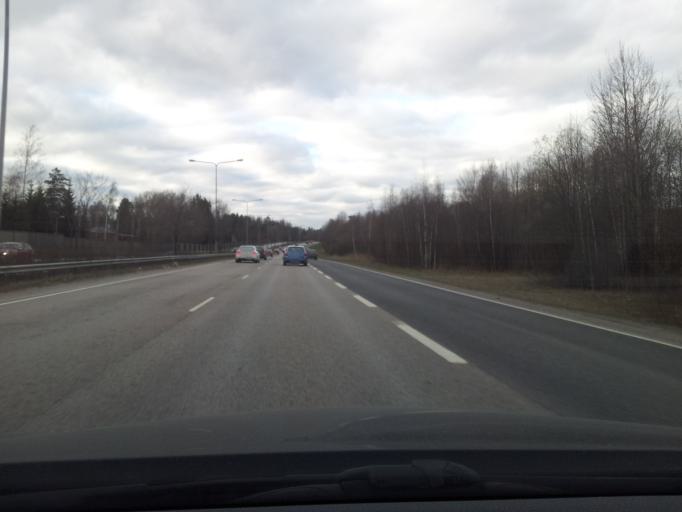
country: FI
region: Uusimaa
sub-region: Helsinki
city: Otaniemi
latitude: 60.1905
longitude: 24.8074
